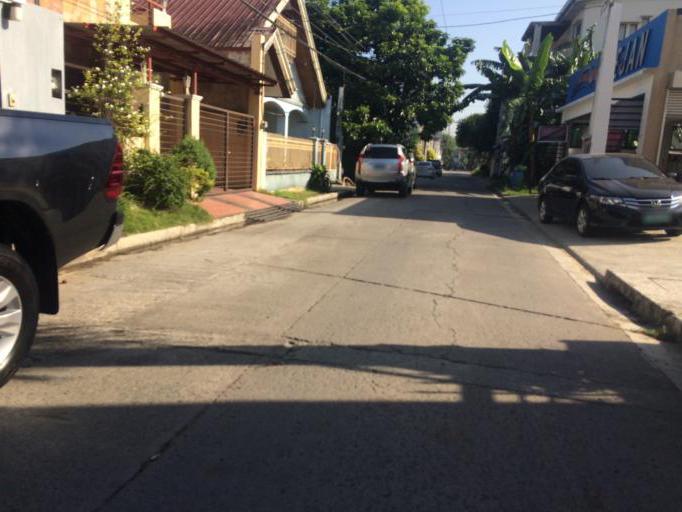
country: PH
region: Calabarzon
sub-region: Province of Rizal
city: Taytay
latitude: 14.5528
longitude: 121.1086
